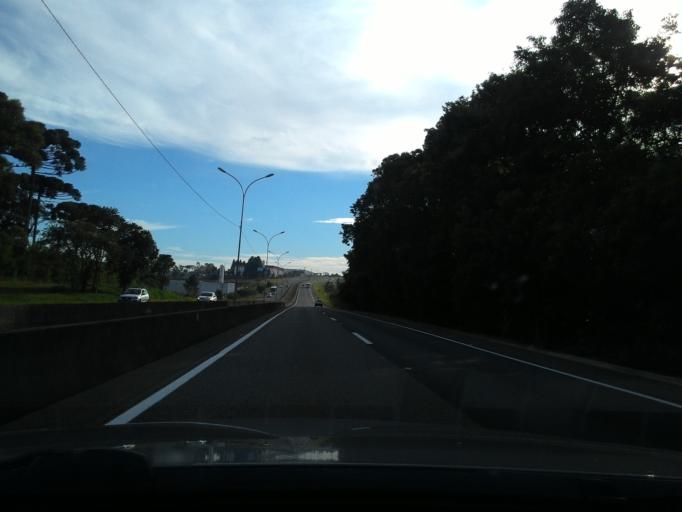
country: BR
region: Parana
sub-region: Quatro Barras
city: Quatro Barras
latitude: -25.3531
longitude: -49.0630
